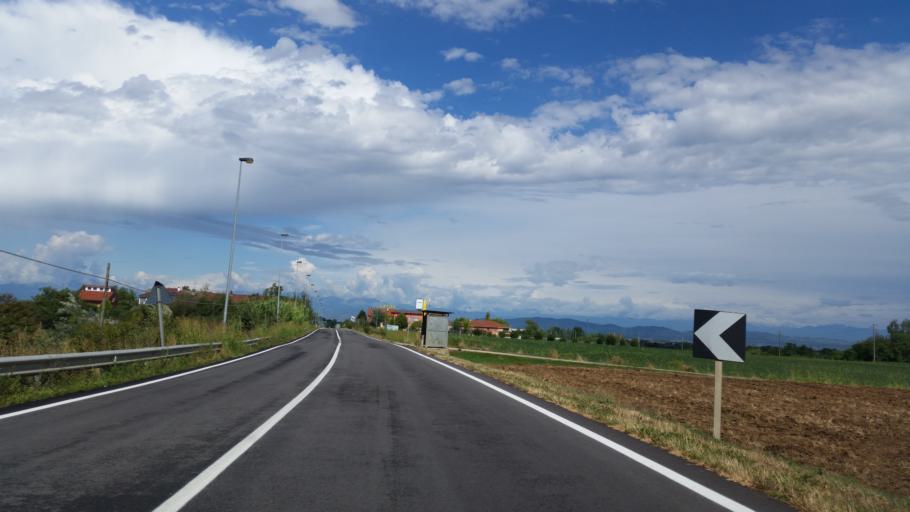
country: IT
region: Piedmont
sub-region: Provincia di Torino
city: Pralormo
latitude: 44.8708
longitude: 7.8949
